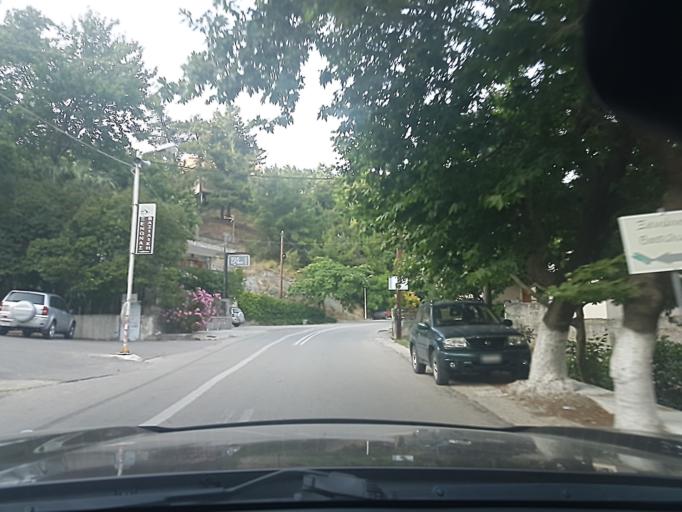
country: GR
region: Central Greece
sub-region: Nomos Evvoias
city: Yimnon
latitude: 38.5825
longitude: 23.8370
